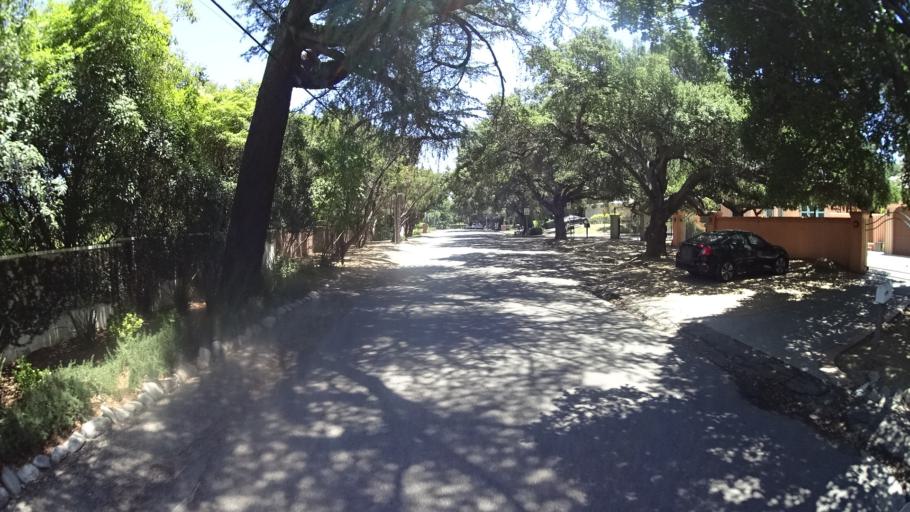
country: US
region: California
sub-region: Los Angeles County
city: Sherman Oaks
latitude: 34.1529
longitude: -118.4802
